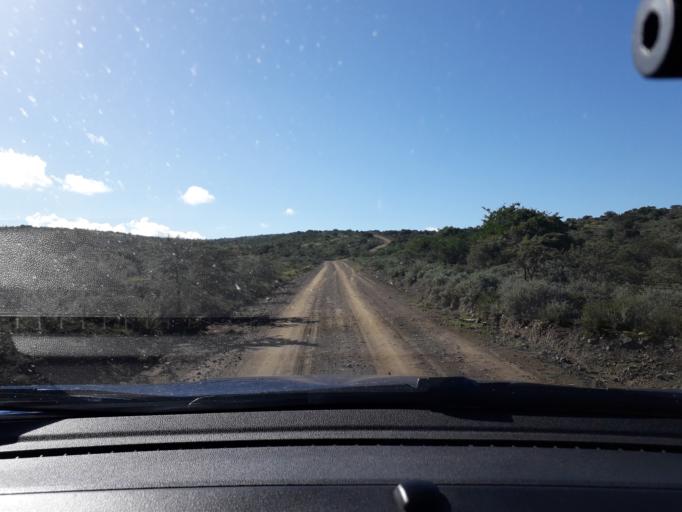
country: ZA
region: Eastern Cape
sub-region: Buffalo City Metropolitan Municipality
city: Bhisho
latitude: -33.1215
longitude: 27.4528
